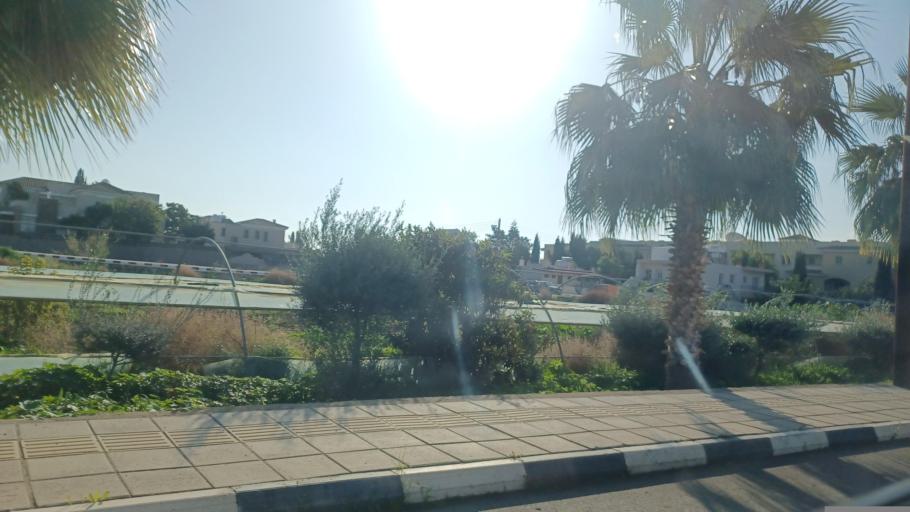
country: CY
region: Pafos
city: Paphos
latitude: 34.7150
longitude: 32.5290
